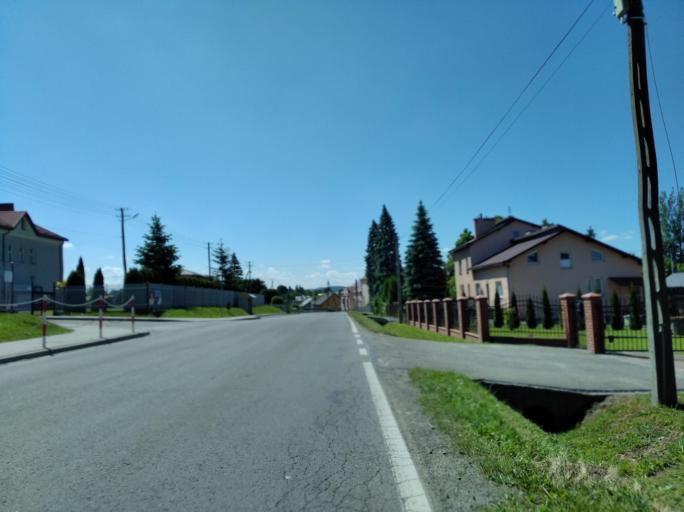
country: PL
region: Subcarpathian Voivodeship
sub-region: Powiat krosnienski
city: Chorkowka
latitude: 49.6657
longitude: 21.6904
